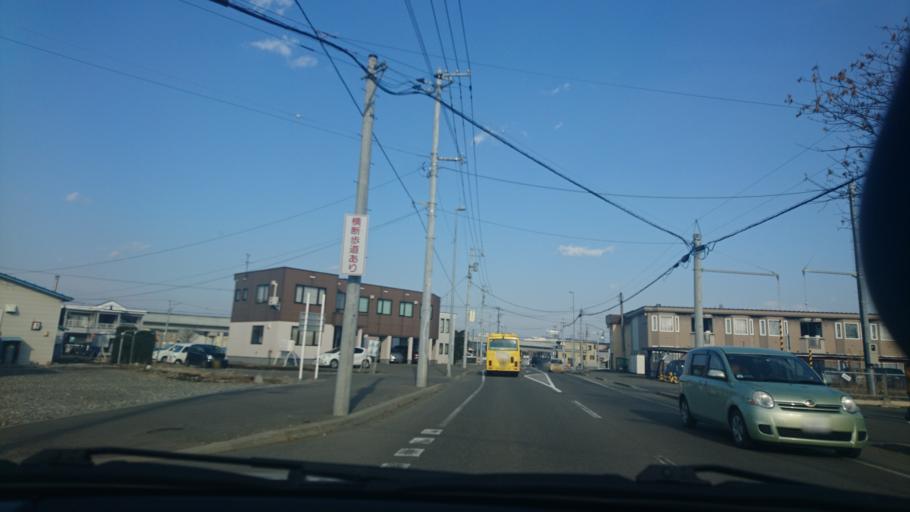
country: JP
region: Hokkaido
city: Obihiro
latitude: 42.9248
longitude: 143.1845
